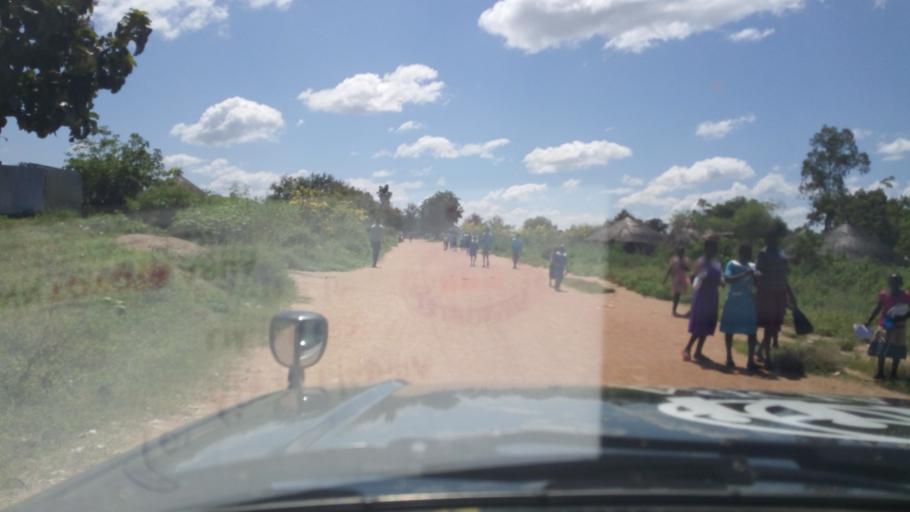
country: UG
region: Northern Region
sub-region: Arua District
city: Arua
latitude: 3.0756
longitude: 31.2830
